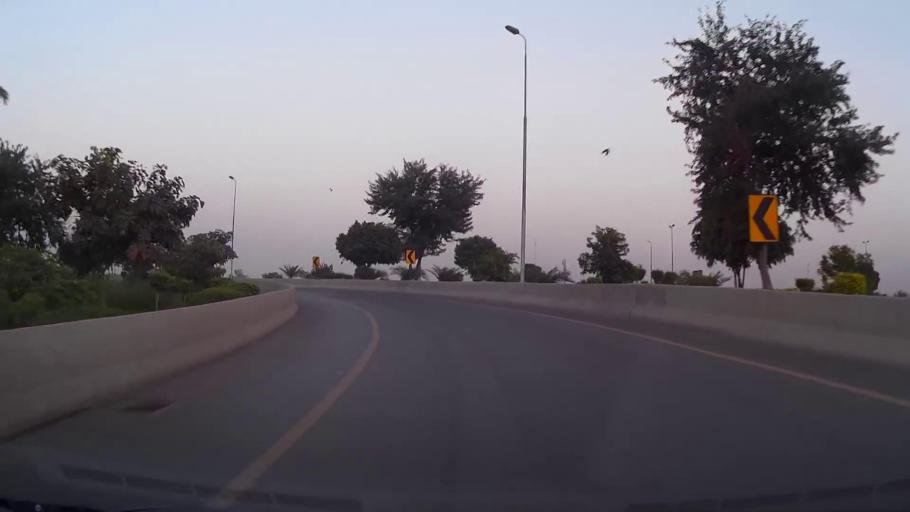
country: PK
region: Punjab
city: Lahore
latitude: 31.6047
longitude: 74.2989
